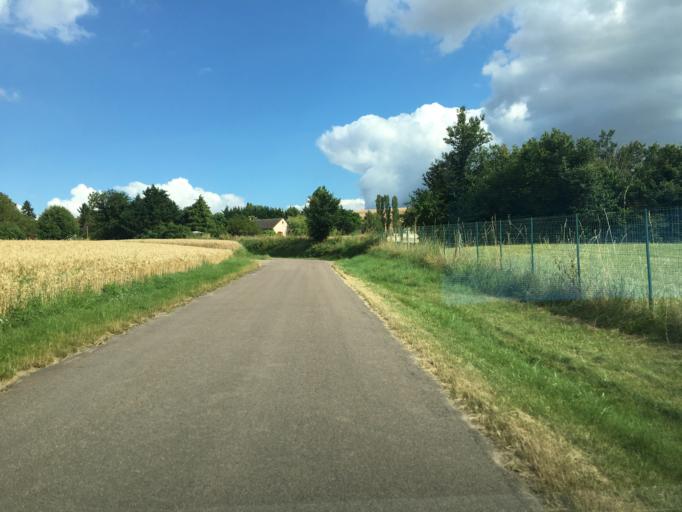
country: FR
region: Bourgogne
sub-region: Departement de l'Yonne
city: Aillant-sur-Tholon
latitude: 47.8238
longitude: 3.3802
